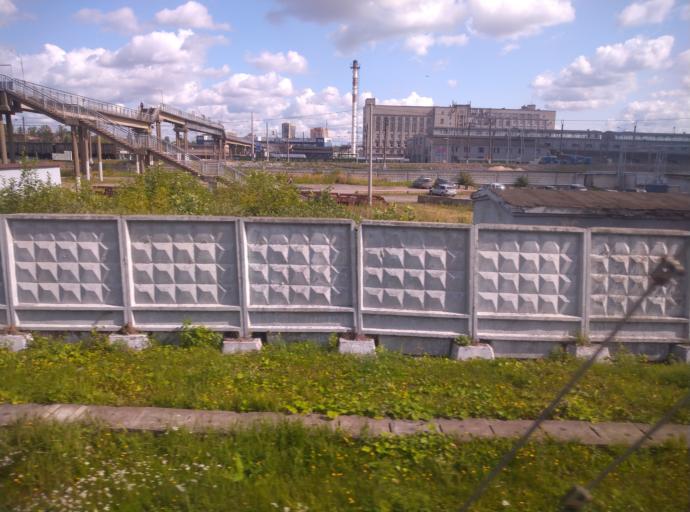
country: RU
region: St.-Petersburg
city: Obukhovo
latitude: 59.8778
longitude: 30.4094
